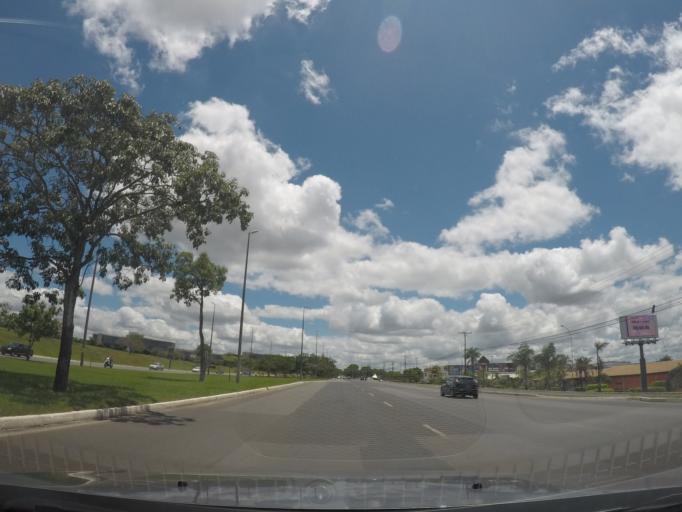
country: BR
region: Federal District
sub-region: Brasilia
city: Brasilia
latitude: -15.8184
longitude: -47.8775
